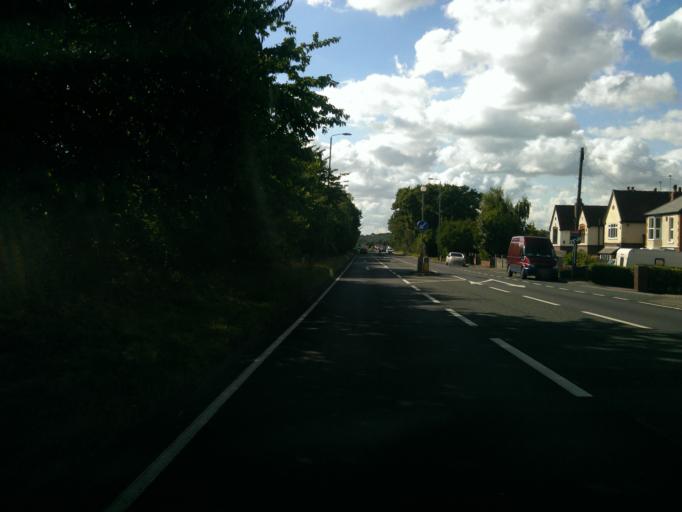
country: GB
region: England
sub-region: Warwickshire
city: Atherstone
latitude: 52.5882
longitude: -1.5829
